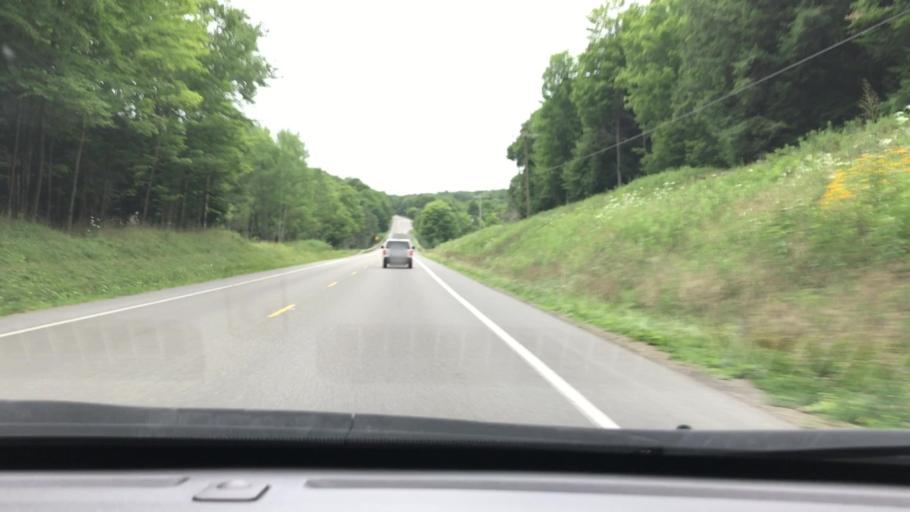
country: US
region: Pennsylvania
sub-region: McKean County
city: Kane
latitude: 41.6936
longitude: -78.6907
